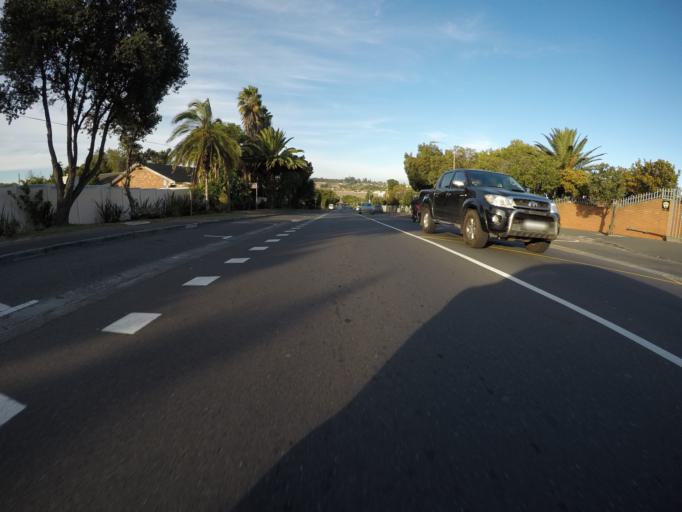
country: ZA
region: Western Cape
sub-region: City of Cape Town
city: Kraaifontein
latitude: -33.8630
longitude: 18.6613
